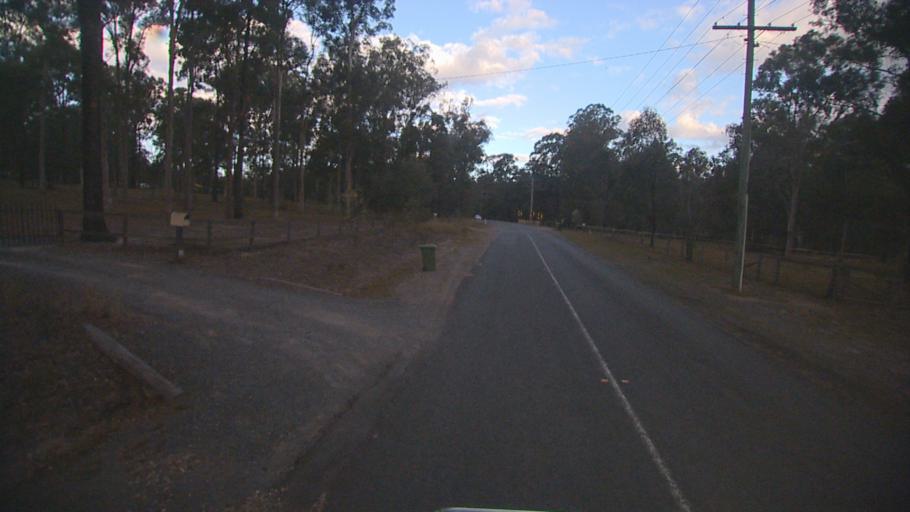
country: AU
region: Queensland
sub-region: Logan
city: Chambers Flat
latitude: -27.7892
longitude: 153.1362
